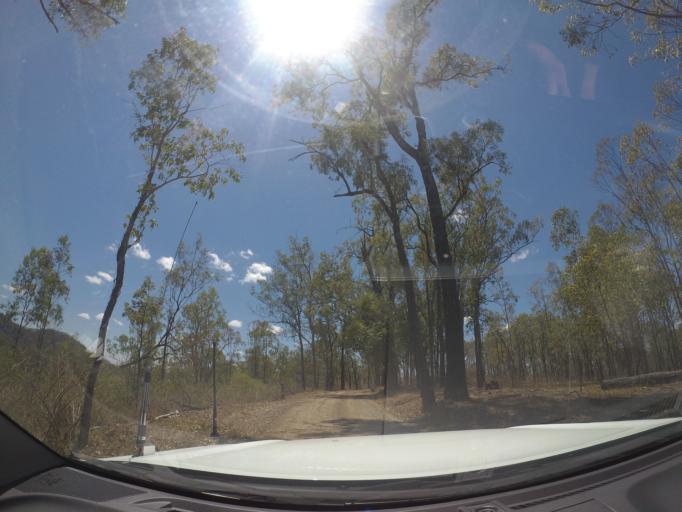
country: AU
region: Queensland
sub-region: Ipswich
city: Deebing Heights
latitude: -27.8292
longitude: 152.8333
